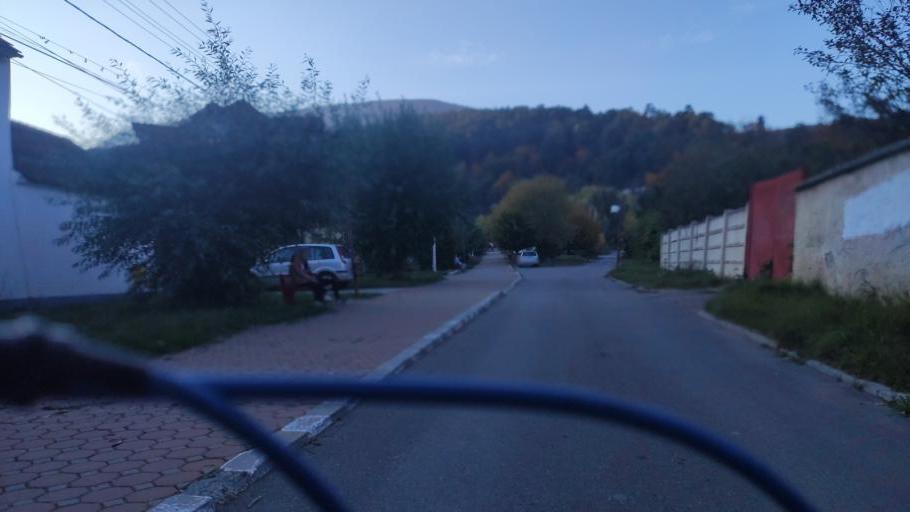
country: RO
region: Brasov
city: Codlea
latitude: 45.7003
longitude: 25.4413
